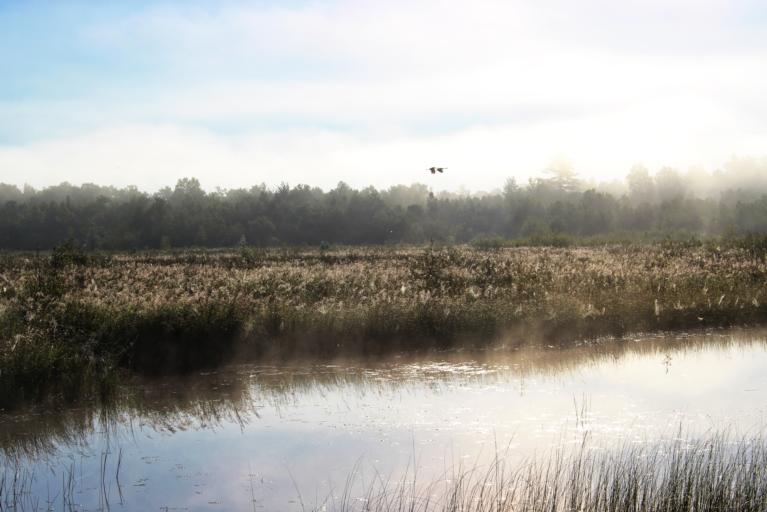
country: US
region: Wisconsin
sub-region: Vilas County
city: Eagle River
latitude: 45.8159
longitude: -89.1912
